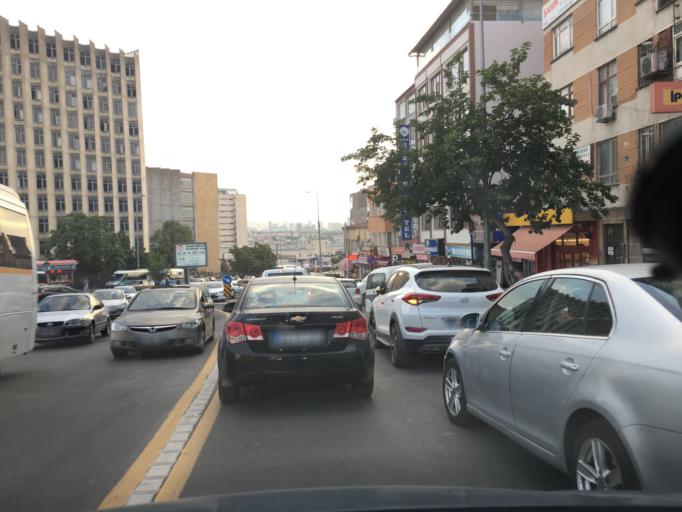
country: TR
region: Ankara
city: Ankara
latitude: 39.9341
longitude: 32.8614
